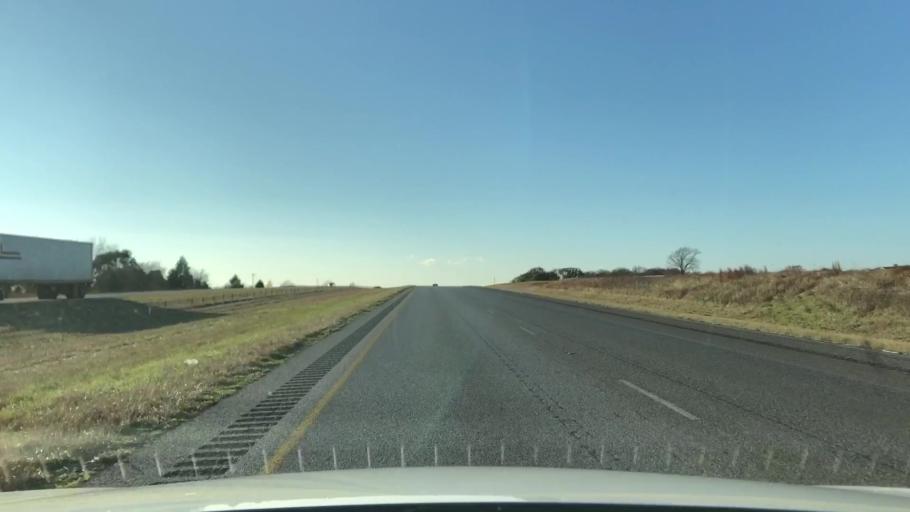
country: US
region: Texas
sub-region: Fayette County
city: Schulenburg
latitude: 29.6892
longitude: -96.9587
